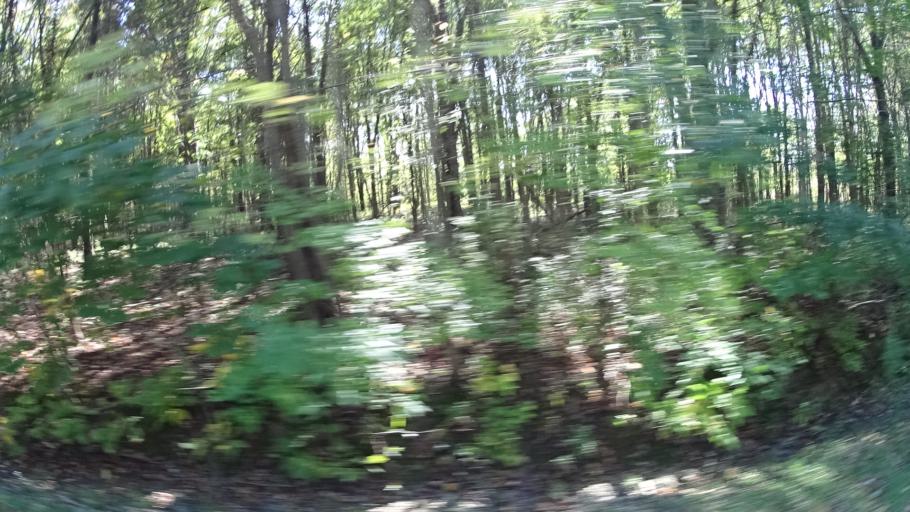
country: US
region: Ohio
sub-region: Lorain County
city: Vermilion-on-the-Lake
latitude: 41.4122
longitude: -82.3356
